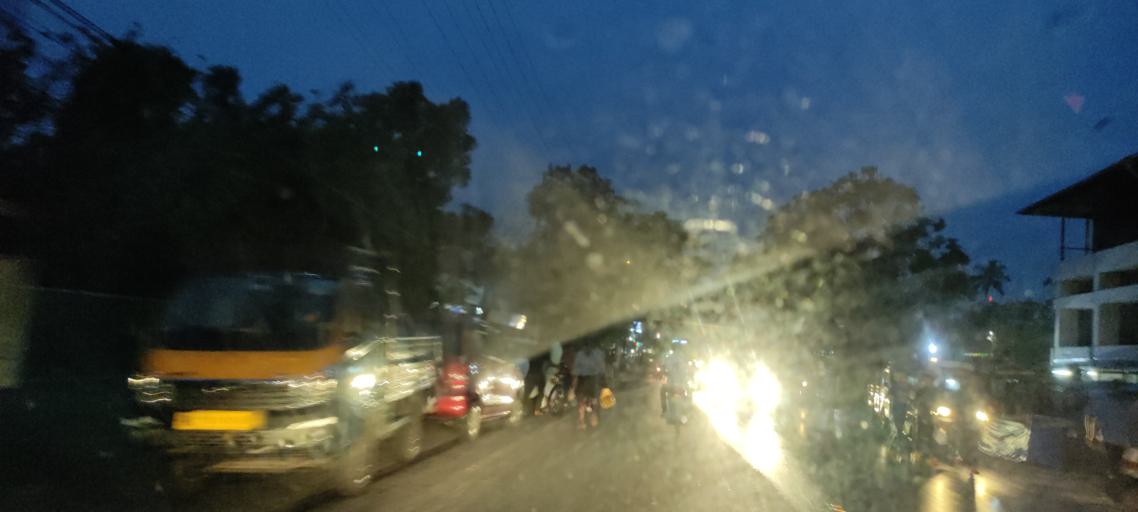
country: IN
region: Kerala
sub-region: Alappuzha
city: Arukutti
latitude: 9.8805
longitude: 76.3030
